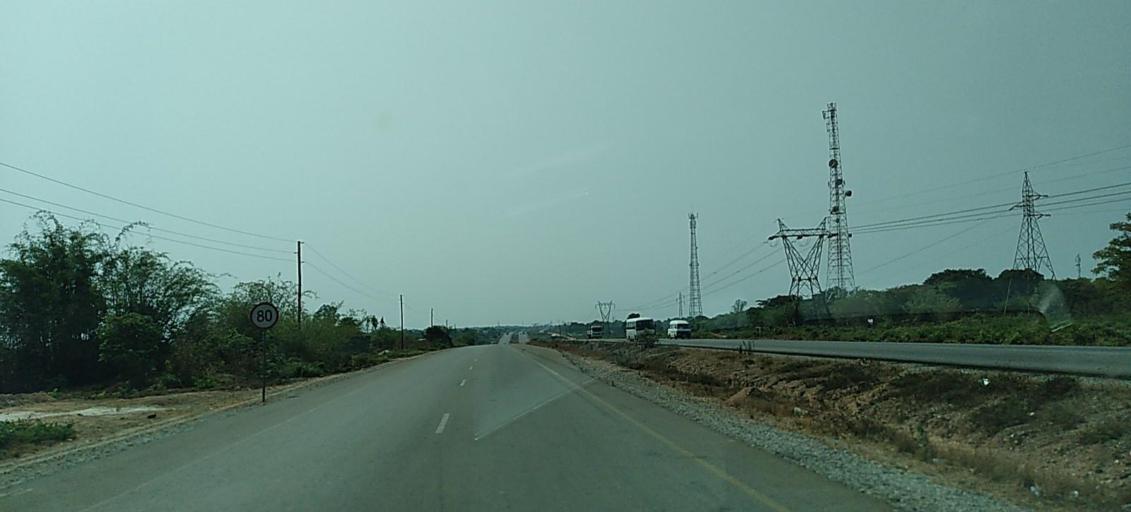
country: ZM
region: Copperbelt
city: Chingola
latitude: -12.5939
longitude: 27.9536
